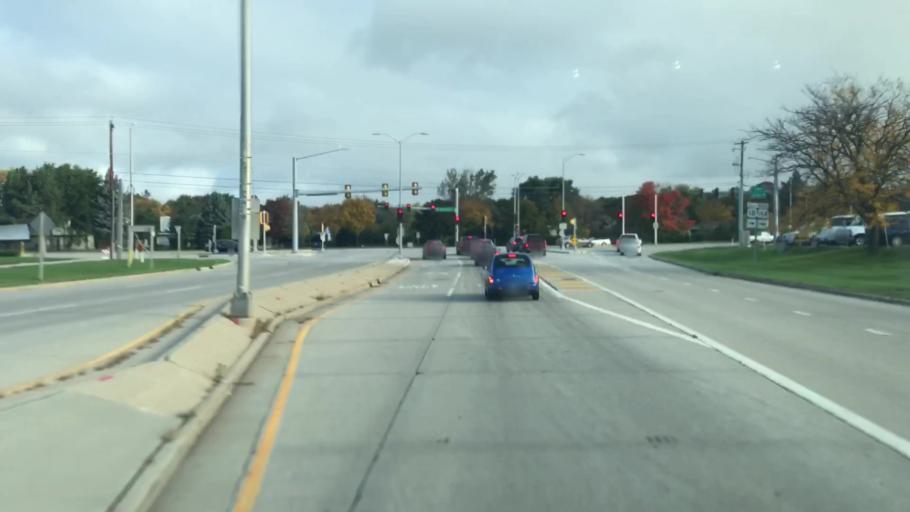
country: US
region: Wisconsin
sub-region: Waukesha County
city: Waukesha
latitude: 43.0250
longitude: -88.2003
